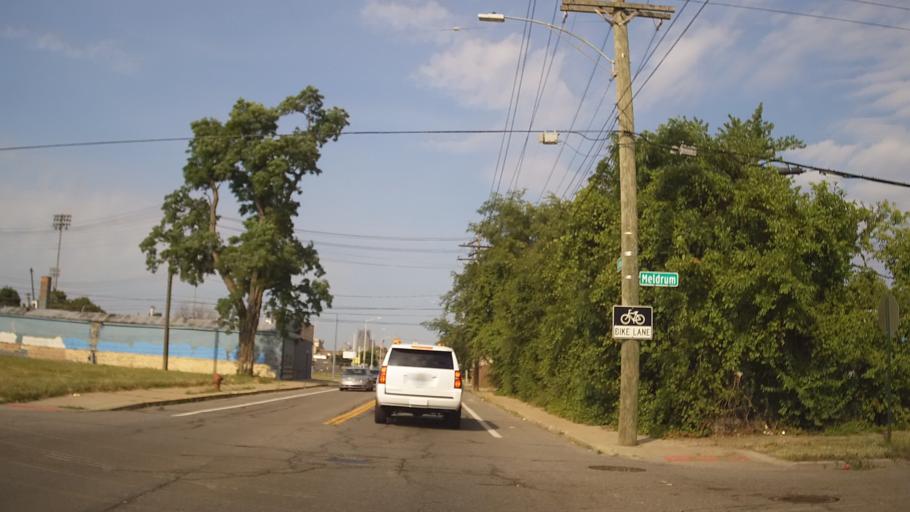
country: US
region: Michigan
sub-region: Wayne County
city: Detroit
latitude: 42.3475
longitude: -83.0108
